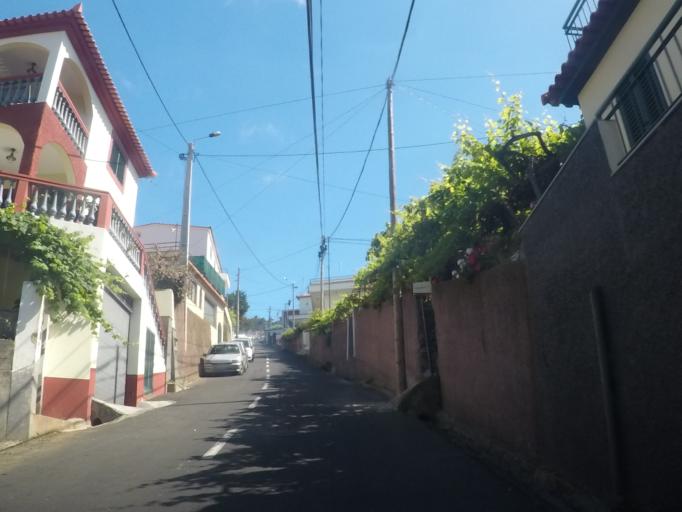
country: PT
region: Madeira
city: Camara de Lobos
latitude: 32.6707
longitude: -16.9649
